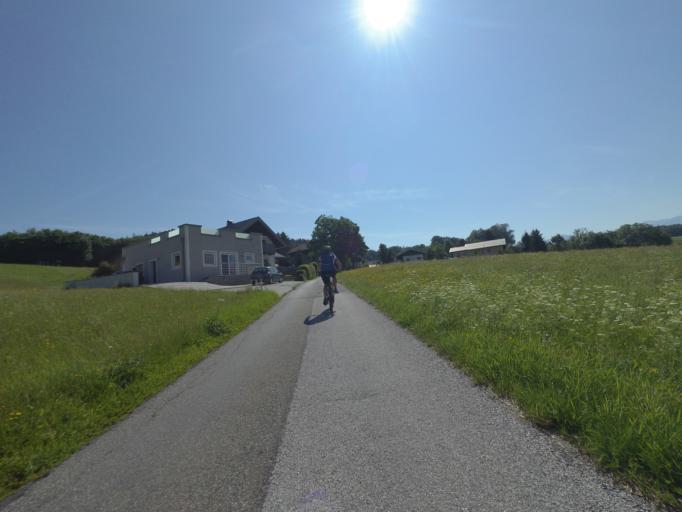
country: AT
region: Salzburg
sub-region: Politischer Bezirk Hallein
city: Adnet
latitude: 47.6878
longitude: 13.1211
